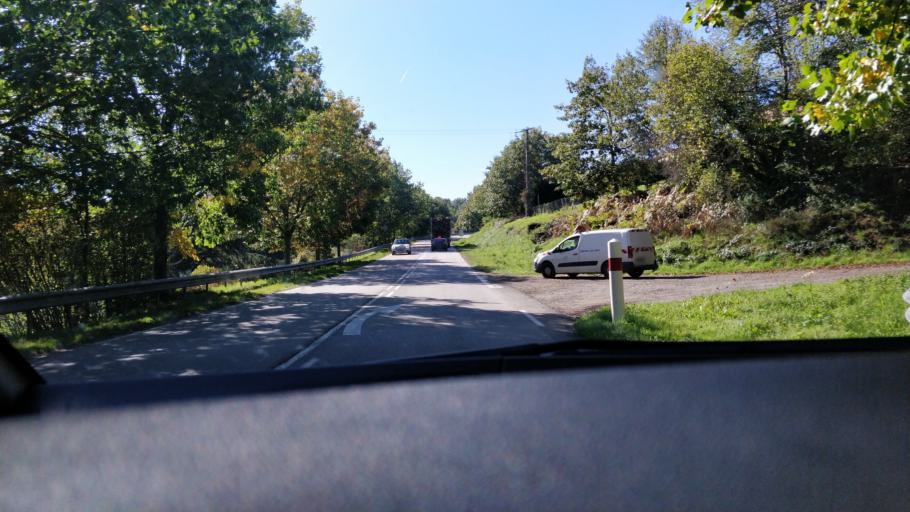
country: FR
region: Limousin
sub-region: Departement de la Haute-Vienne
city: Saint-Leonard-de-Noblat
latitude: 45.8478
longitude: 1.4942
